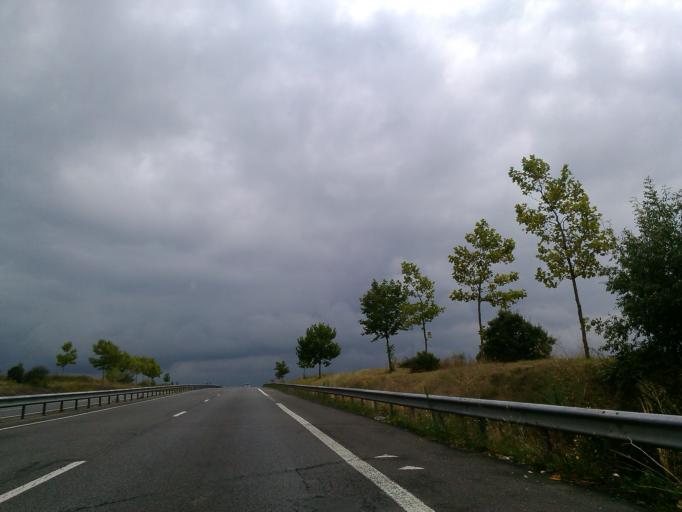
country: FR
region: Poitou-Charentes
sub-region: Departement de la Charente
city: Gensac-la-Pallue
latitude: 45.6704
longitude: -0.2556
